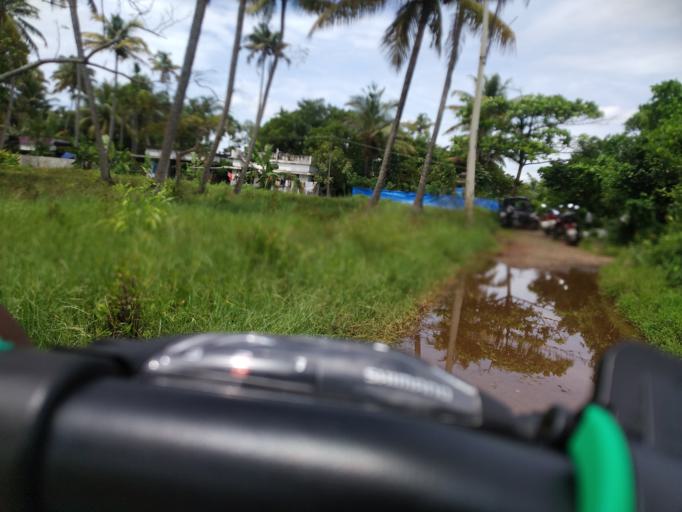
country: IN
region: Kerala
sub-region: Ernakulam
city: Elur
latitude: 10.0821
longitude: 76.2211
